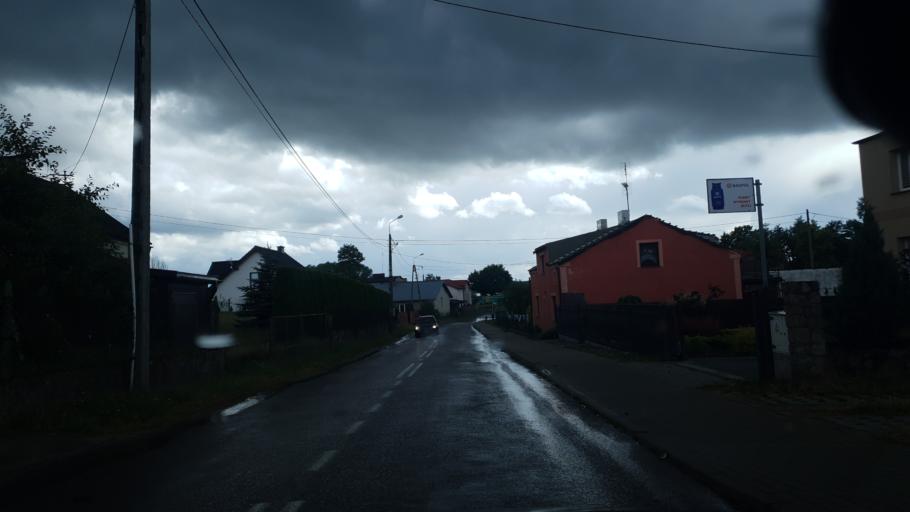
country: PL
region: Pomeranian Voivodeship
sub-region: Powiat kartuski
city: Stezyca
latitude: 54.2073
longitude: 17.9565
